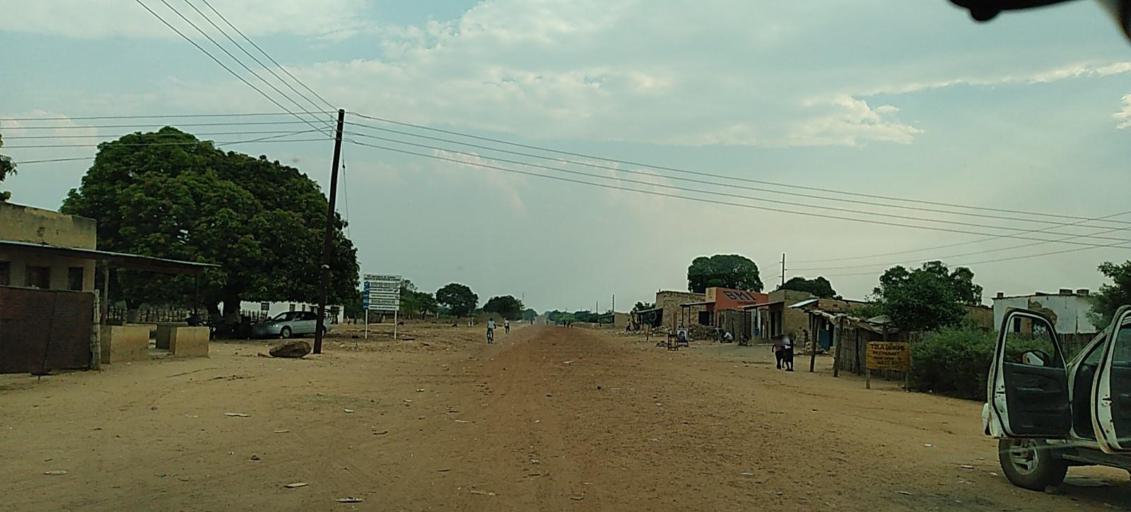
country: ZM
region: North-Western
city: Kabompo
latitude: -13.8614
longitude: 23.6719
